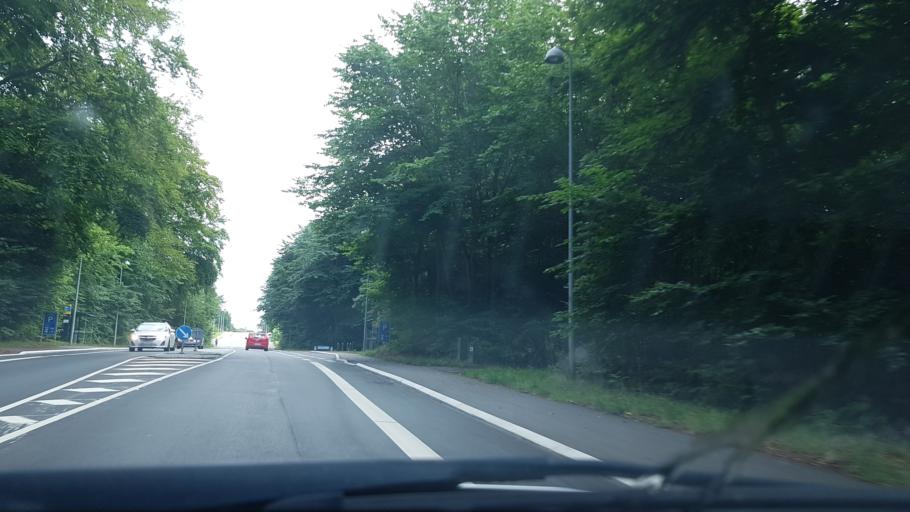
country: DK
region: Capital Region
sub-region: Fredensborg Kommune
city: Kokkedal
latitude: 55.8989
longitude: 12.4849
